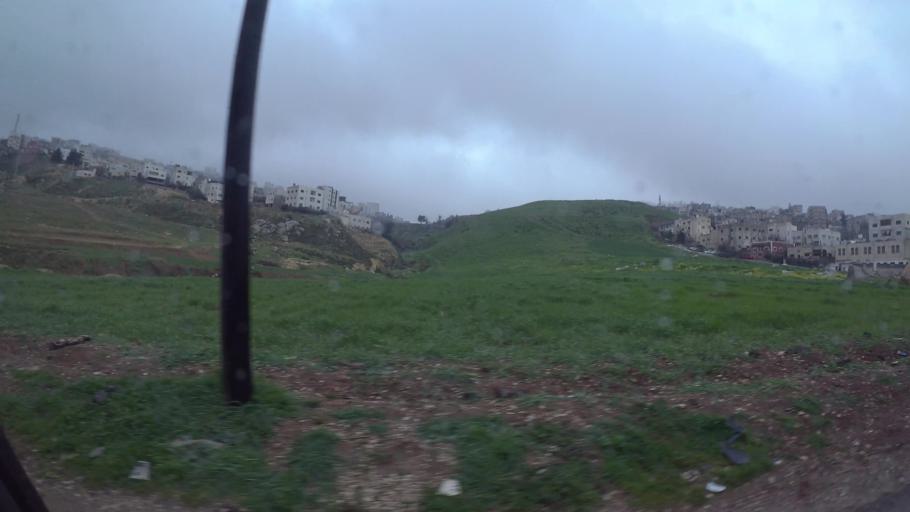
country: JO
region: Amman
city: Al Jubayhah
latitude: 32.0352
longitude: 35.8379
